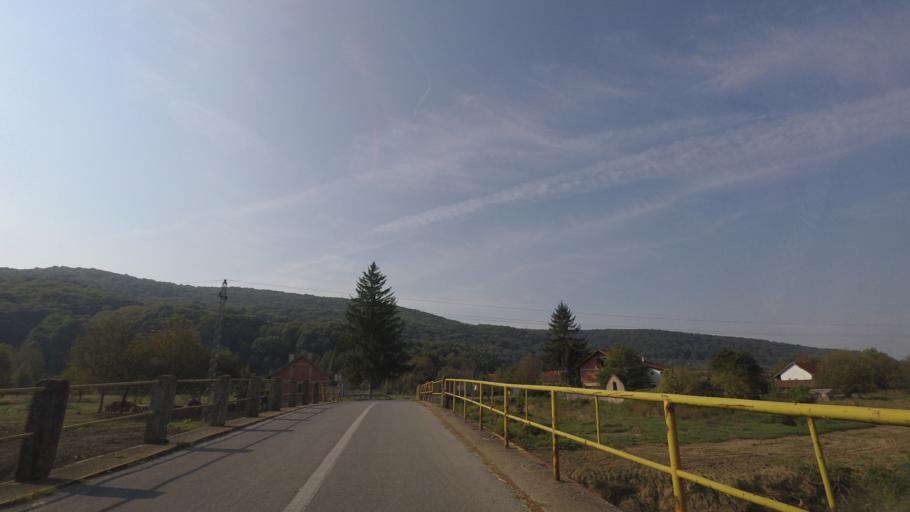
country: HR
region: Pozesko-Slavonska
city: Pakrac
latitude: 45.4574
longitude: 17.2260
